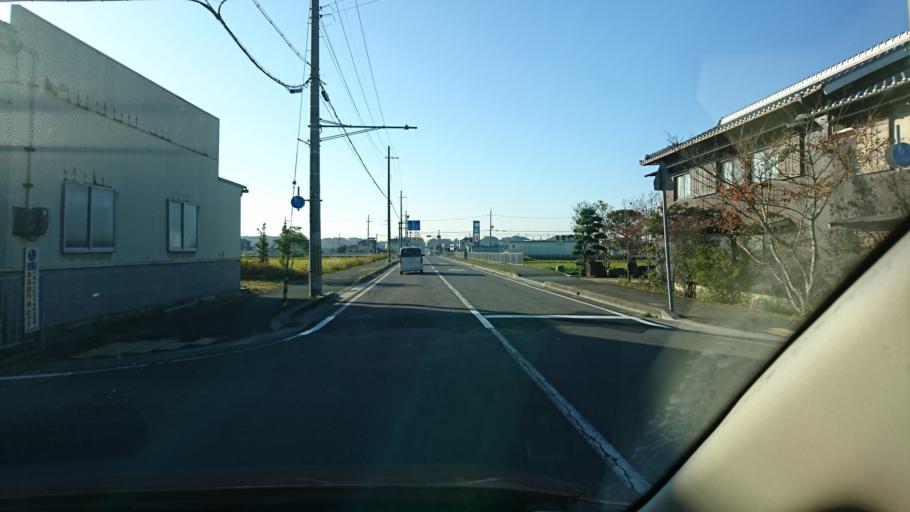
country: JP
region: Hyogo
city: Miki
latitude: 34.7626
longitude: 134.9197
